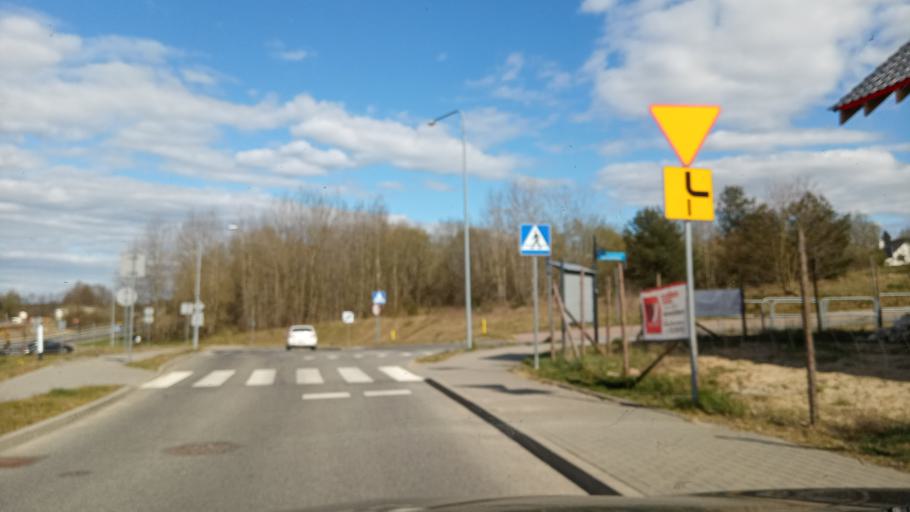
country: PL
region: West Pomeranian Voivodeship
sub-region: Powiat szczecinecki
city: Szczecinek
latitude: 53.7151
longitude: 16.7315
